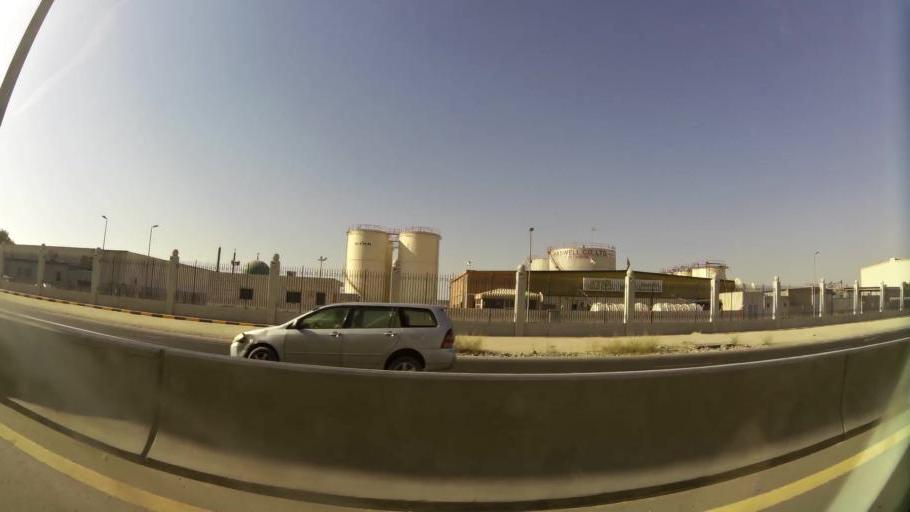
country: AE
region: Ajman
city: Ajman
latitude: 25.3943
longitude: 55.4649
